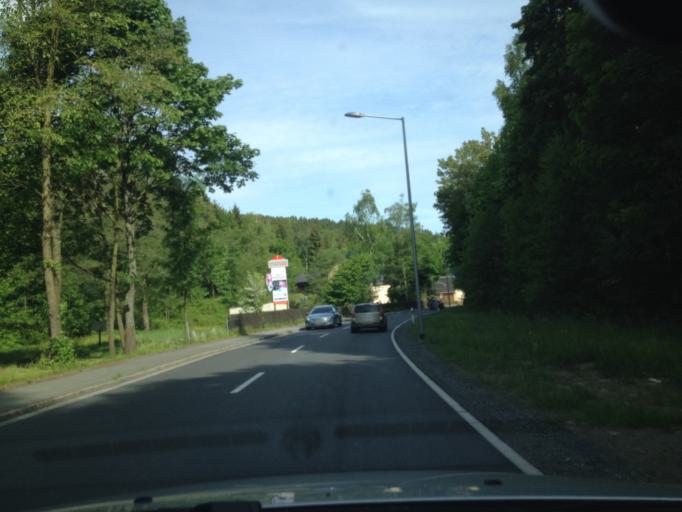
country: DE
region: Saxony
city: Ehrenfriedersdorf
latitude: 50.6596
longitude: 12.9676
